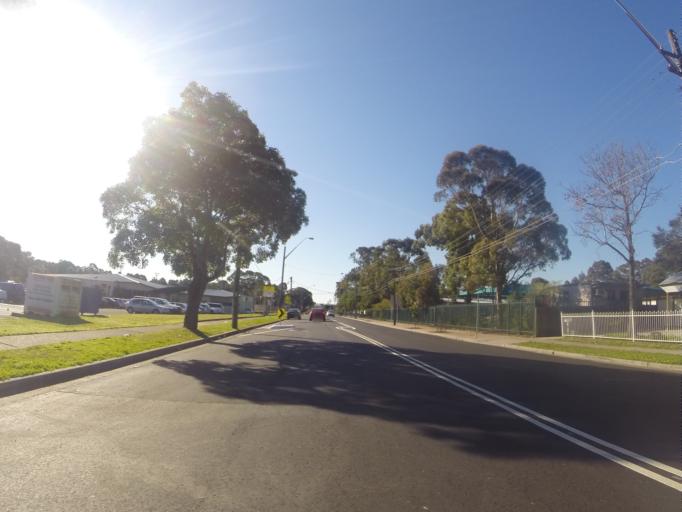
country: AU
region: New South Wales
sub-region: Auburn
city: Berala
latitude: -33.8617
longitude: 151.0189
